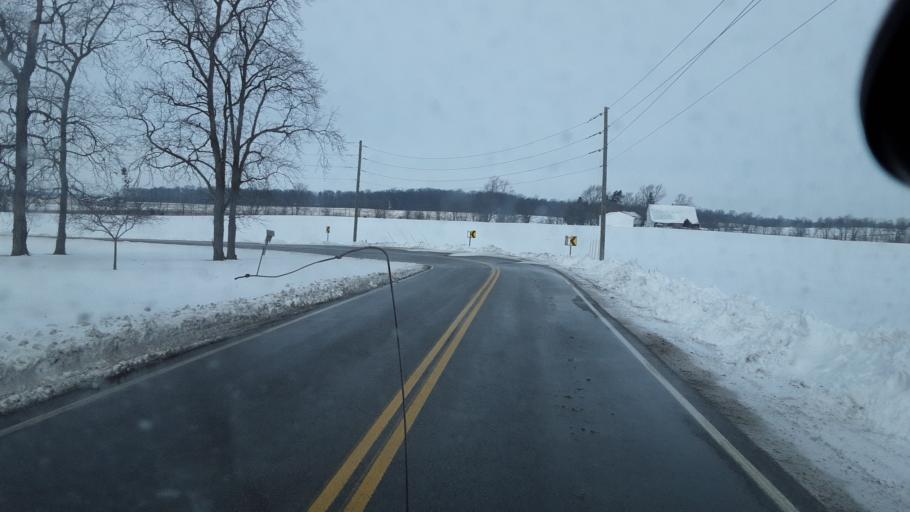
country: US
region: Ohio
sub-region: Union County
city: Marysville
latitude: 40.1823
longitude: -83.3787
